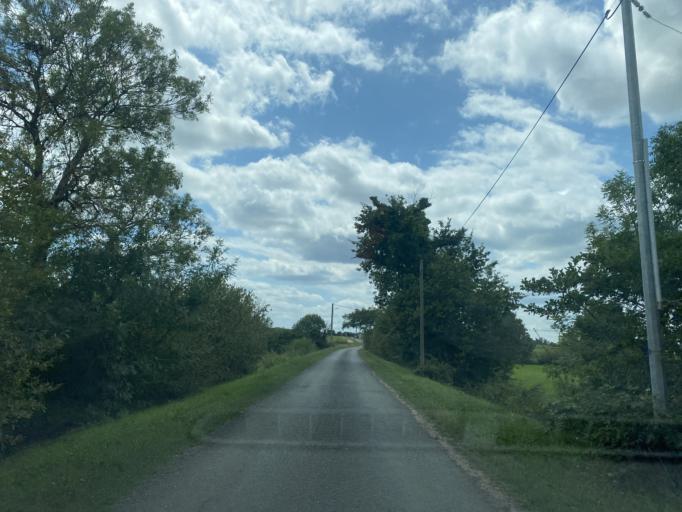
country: FR
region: Aquitaine
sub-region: Departement de la Gironde
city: Soussans
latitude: 45.0629
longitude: -0.6799
